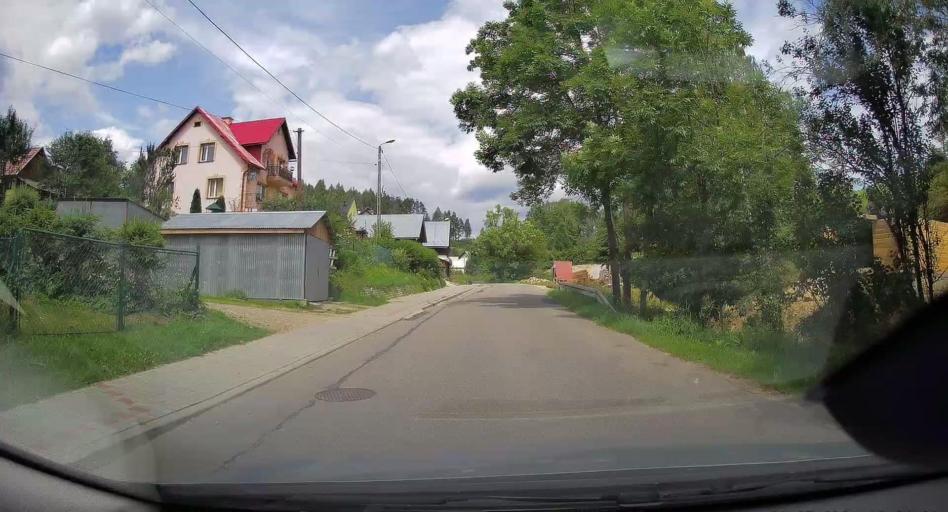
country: PL
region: Lesser Poland Voivodeship
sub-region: Powiat nowosadecki
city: Muszyna
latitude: 49.3805
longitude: 20.8950
